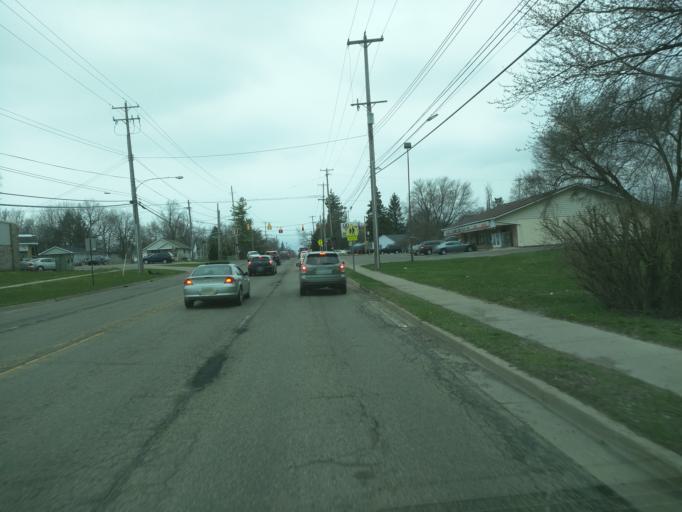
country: US
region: Michigan
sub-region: Ingham County
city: Lansing
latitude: 42.6831
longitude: -84.5614
